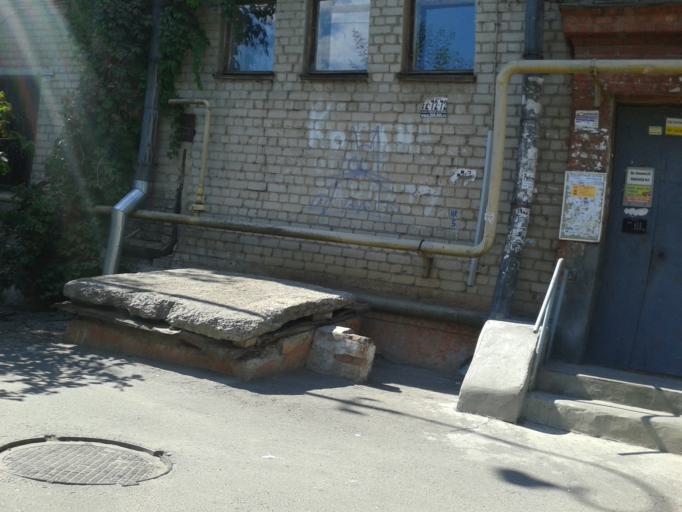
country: RU
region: Volgograd
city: Volgograd
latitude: 48.7099
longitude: 44.5225
